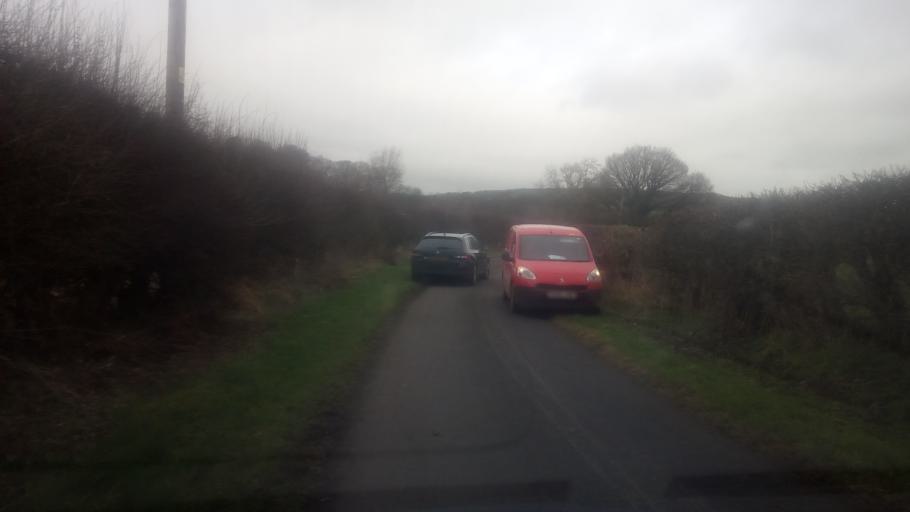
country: GB
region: Scotland
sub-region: The Scottish Borders
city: Jedburgh
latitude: 55.5045
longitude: -2.5368
